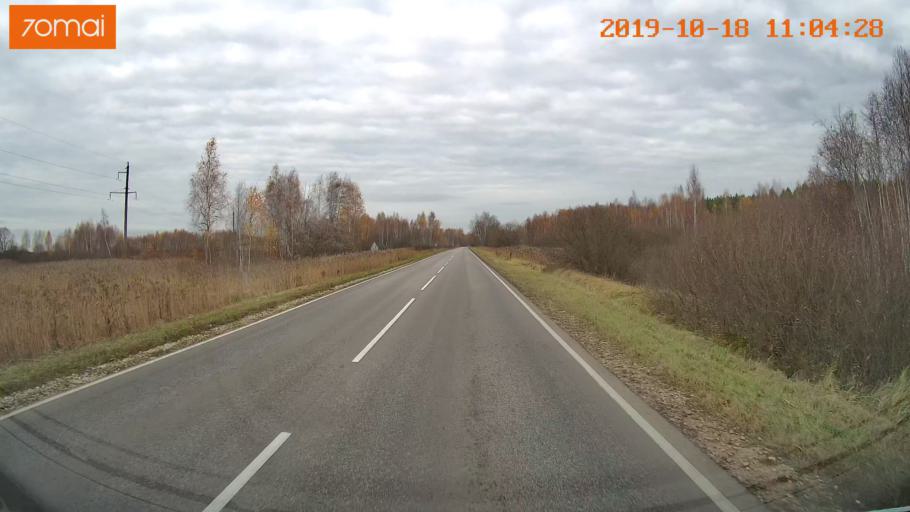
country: RU
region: Tula
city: Yepifan'
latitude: 53.8937
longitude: 38.5474
